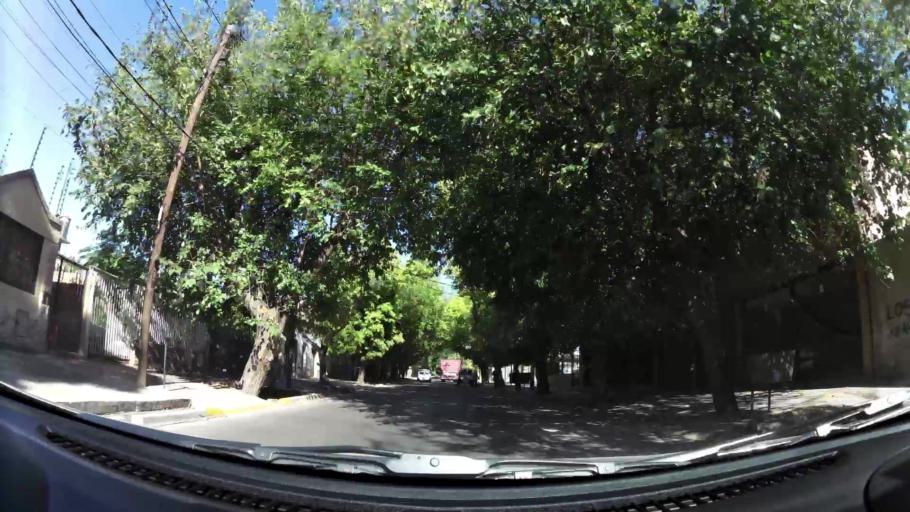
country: AR
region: Mendoza
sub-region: Departamento de Godoy Cruz
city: Godoy Cruz
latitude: -32.9242
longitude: -68.8585
